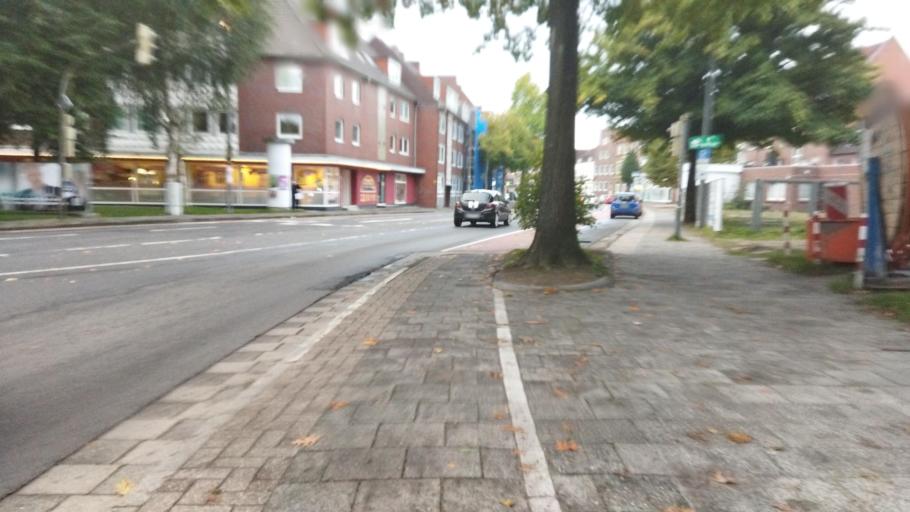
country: DE
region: Lower Saxony
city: Emden
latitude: 53.3736
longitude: 7.2072
